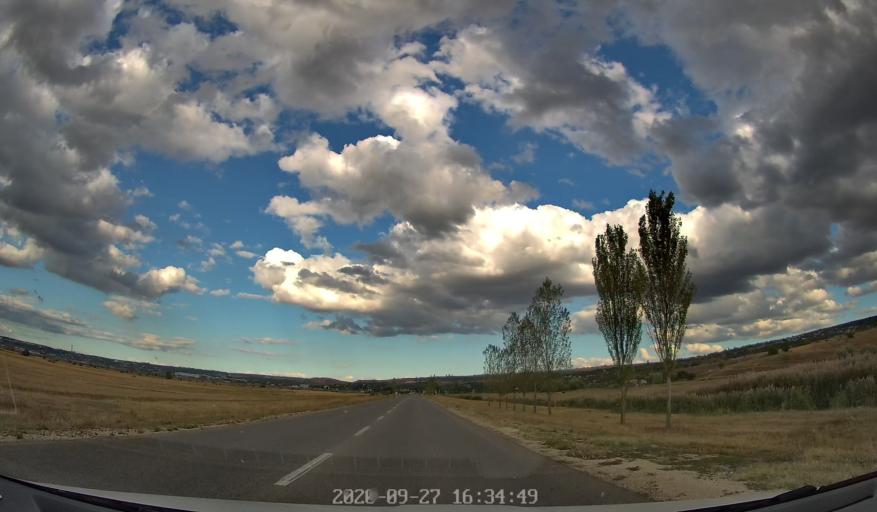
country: MD
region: Orhei
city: Orhei
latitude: 47.3444
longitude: 28.7842
